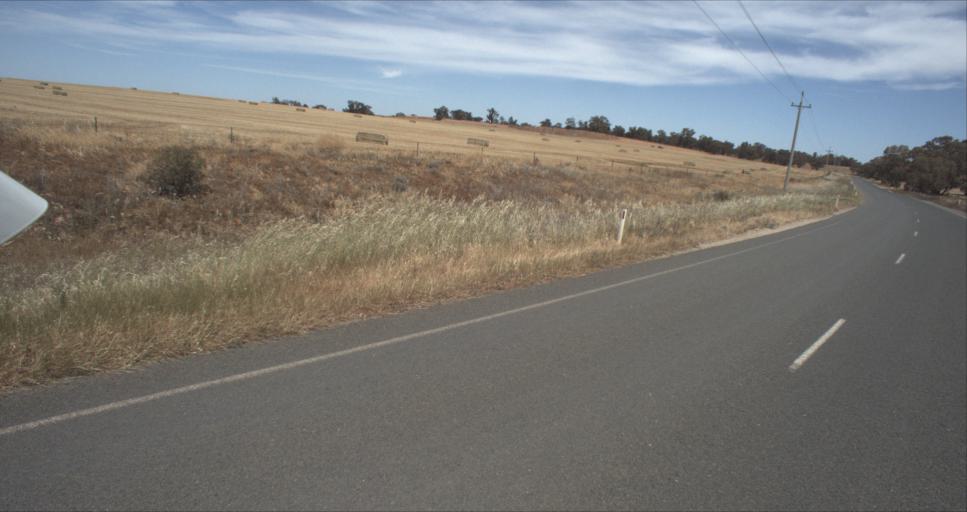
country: AU
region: New South Wales
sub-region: Leeton
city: Leeton
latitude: -34.6533
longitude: 146.4620
